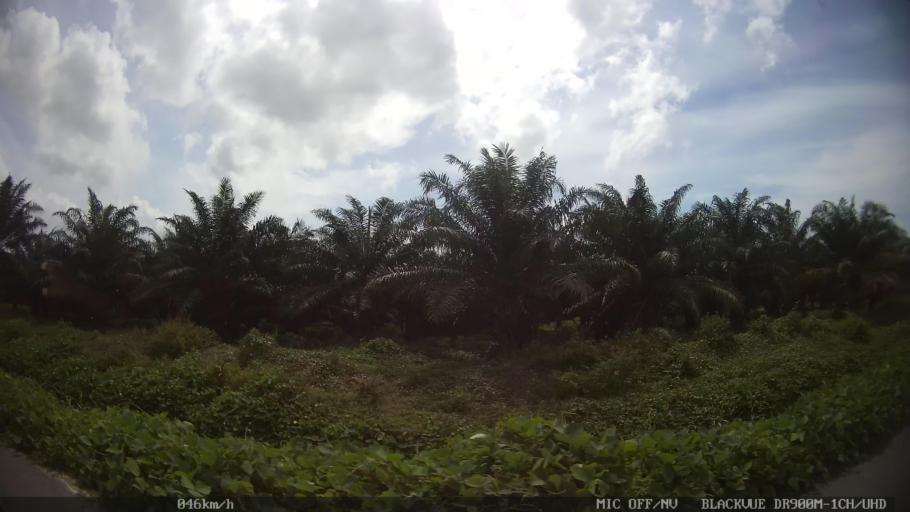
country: ID
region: North Sumatra
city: Percut
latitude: 3.5966
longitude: 98.8393
